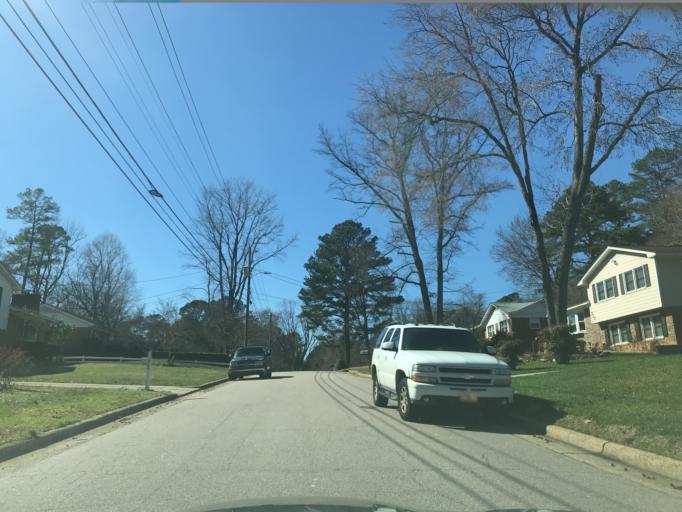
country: US
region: North Carolina
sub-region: Wake County
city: West Raleigh
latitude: 35.8421
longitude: -78.6337
